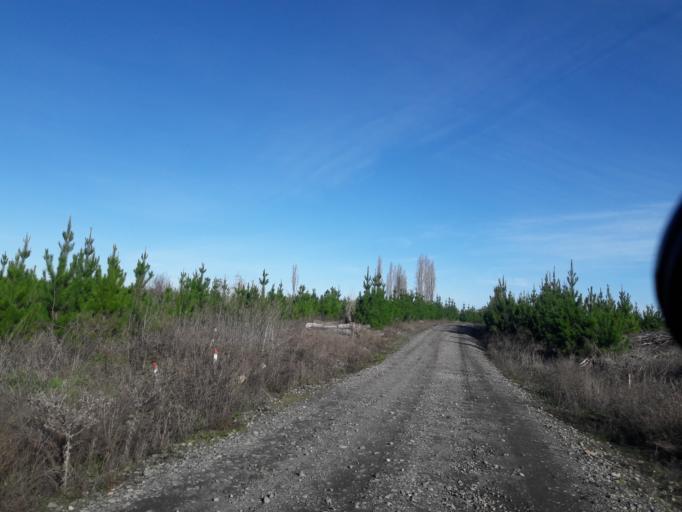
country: CL
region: Biobio
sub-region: Provincia de Biobio
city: Cabrero
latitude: -37.0185
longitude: -72.1881
